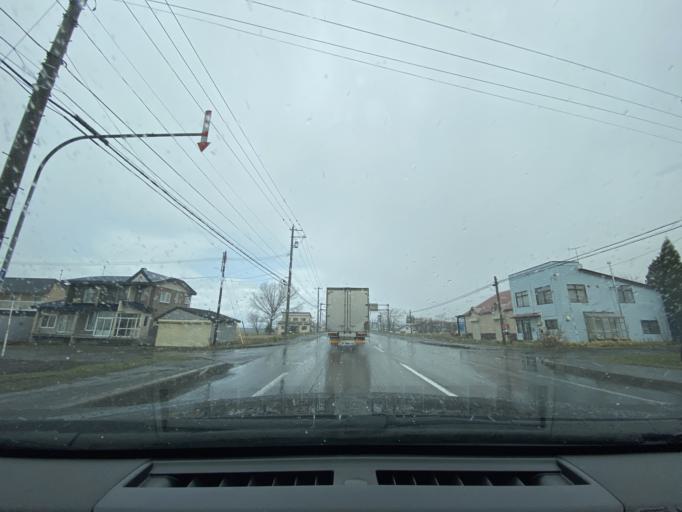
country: JP
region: Hokkaido
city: Takikawa
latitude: 43.6319
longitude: 141.9442
